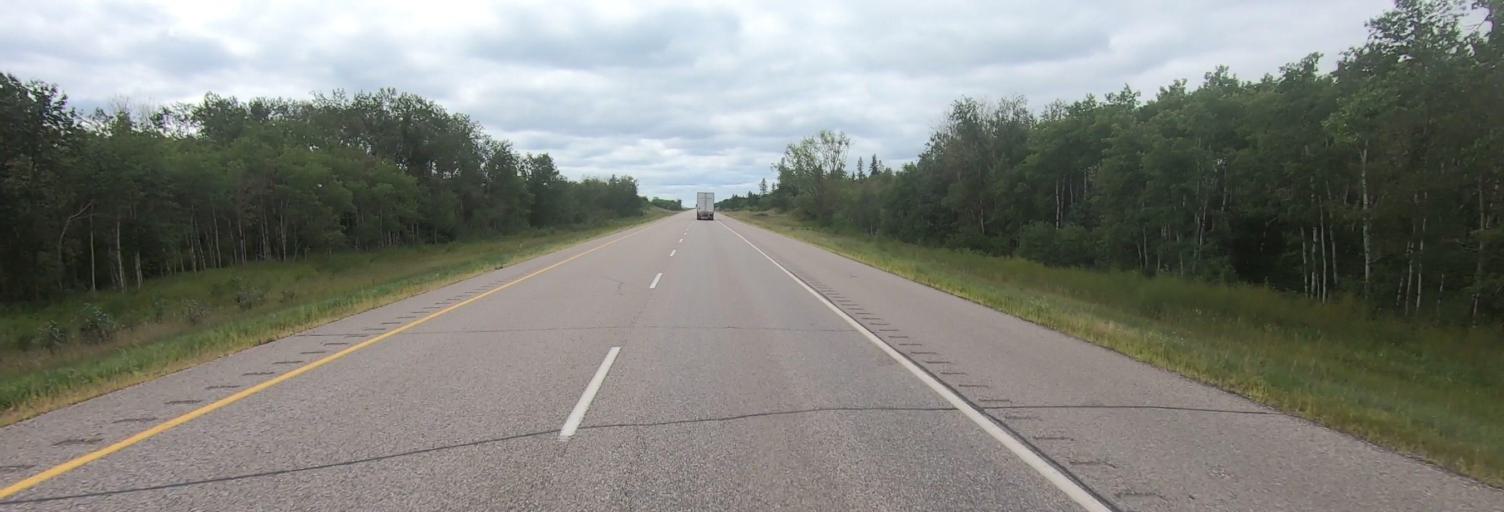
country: CA
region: Manitoba
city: Carberry
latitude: 49.9016
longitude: -99.2543
